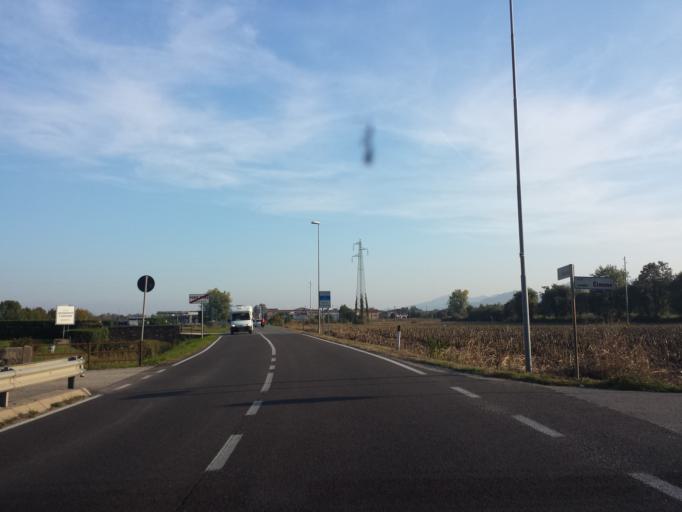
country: IT
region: Veneto
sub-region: Provincia di Vicenza
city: San Vito di Leguzzano
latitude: 45.6964
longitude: 11.3852
